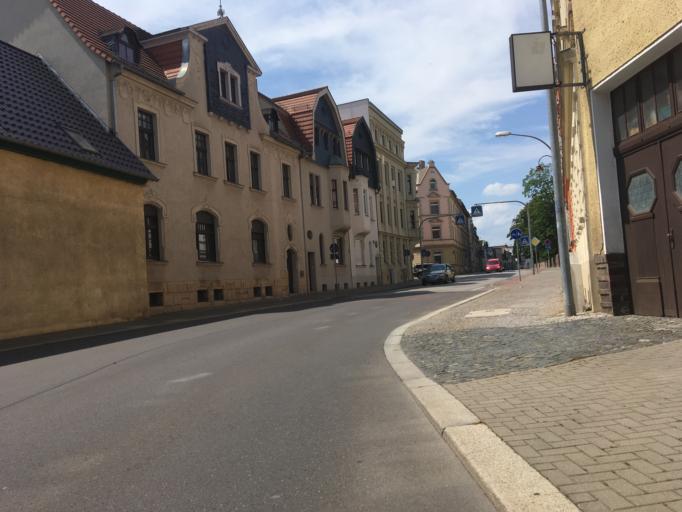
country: DE
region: Saxony-Anhalt
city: Koethen
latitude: 51.7492
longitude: 11.9788
